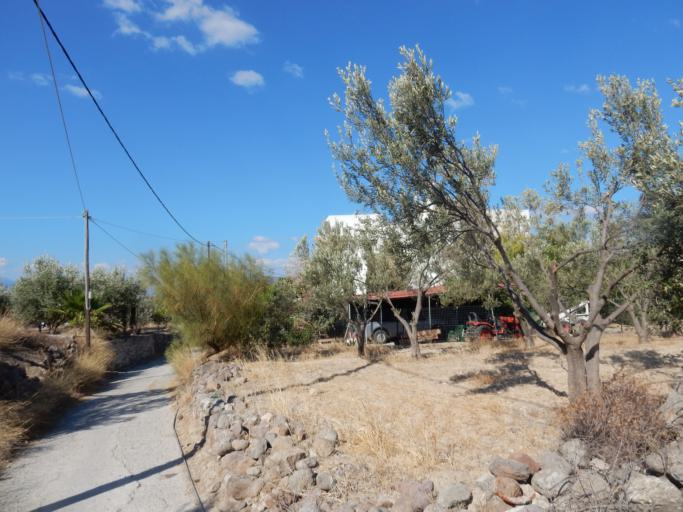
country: GR
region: Attica
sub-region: Nomos Piraios
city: Aegina
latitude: 37.7297
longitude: 23.4475
